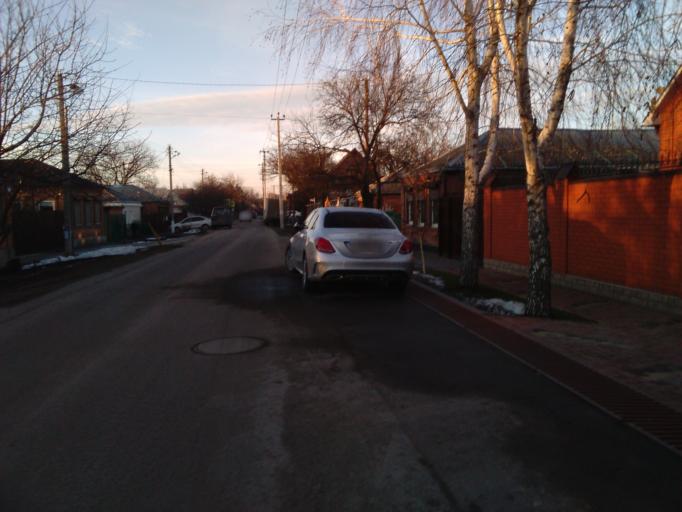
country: RU
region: Rostov
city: Bataysk
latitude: 47.1453
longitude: 39.7428
